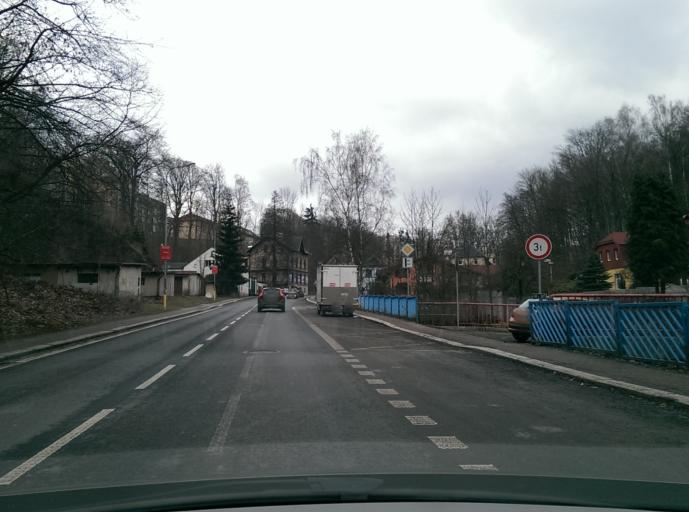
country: CZ
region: Liberecky
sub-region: Okres Jablonec nad Nisou
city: Jablonec nad Nisou
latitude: 50.7284
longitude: 15.1852
